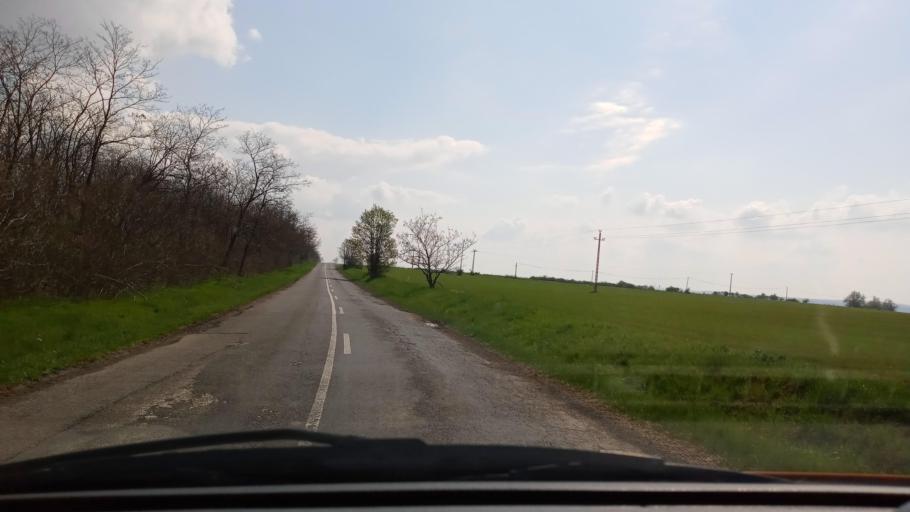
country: HU
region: Baranya
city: Pecsvarad
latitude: 46.1080
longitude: 18.4922
